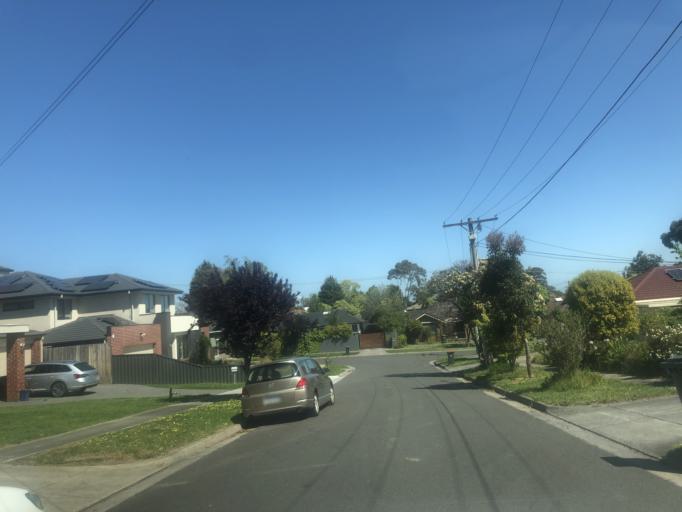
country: AU
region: Victoria
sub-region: Monash
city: Notting Hill
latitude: -37.9022
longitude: 145.1729
